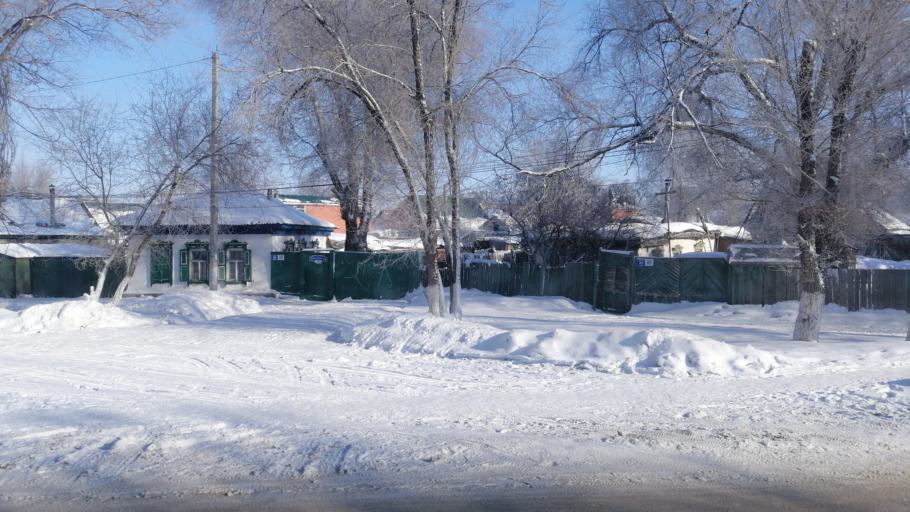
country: KZ
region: Aqtoebe
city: Aqtobe
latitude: 50.2859
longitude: 57.2114
